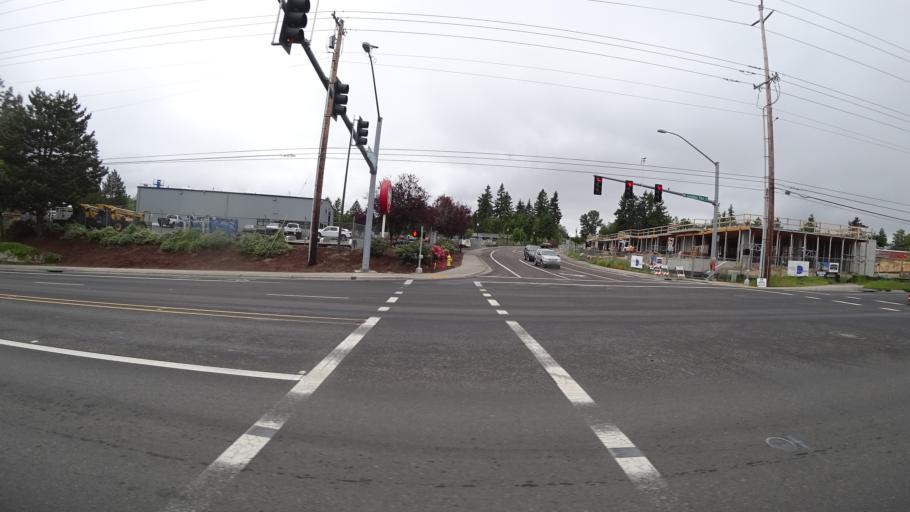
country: US
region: Oregon
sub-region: Washington County
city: Rockcreek
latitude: 45.5303
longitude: -122.8996
